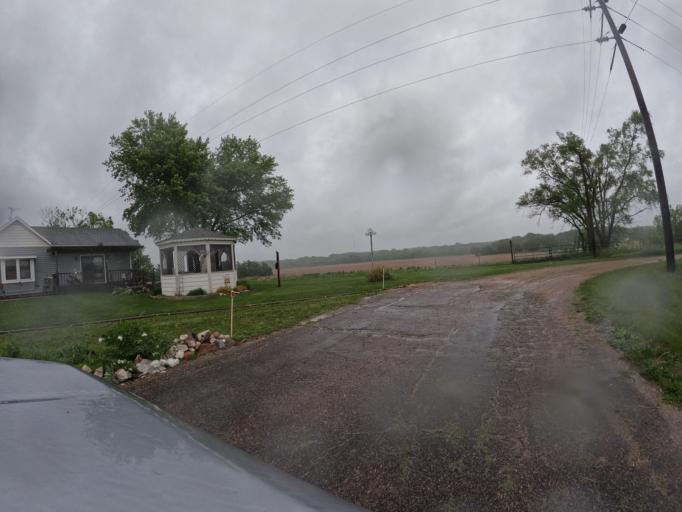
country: US
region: Nebraska
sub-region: Gage County
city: Wymore
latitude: 40.1254
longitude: -96.6547
